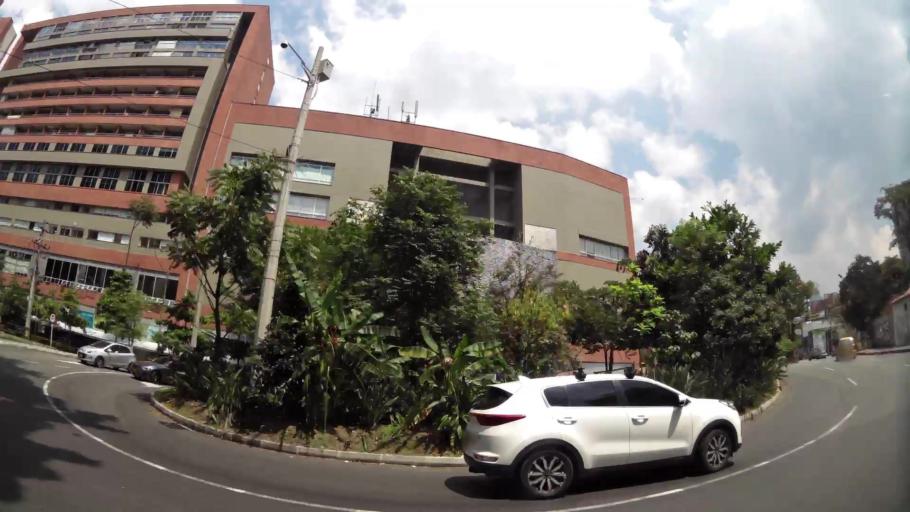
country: CO
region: Antioquia
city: Envigado
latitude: 6.1846
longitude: -75.5802
